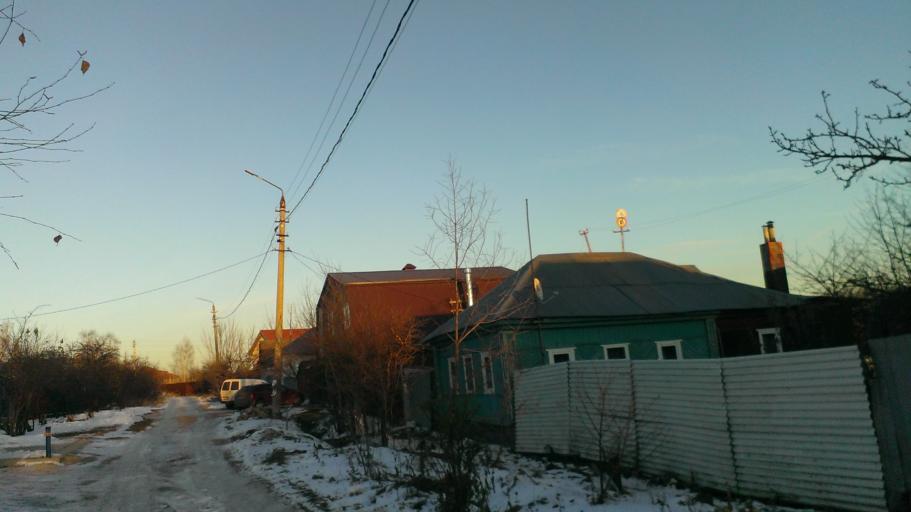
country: RU
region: Tula
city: Tula
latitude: 54.1989
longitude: 37.6974
